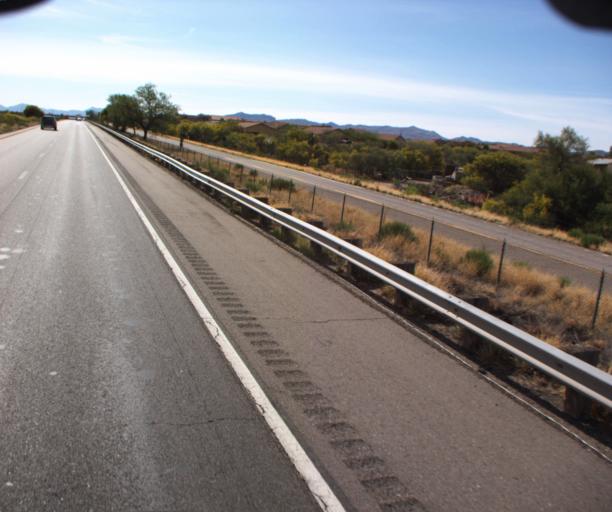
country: US
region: Arizona
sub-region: Pima County
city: Vail
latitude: 32.0120
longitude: -110.6981
